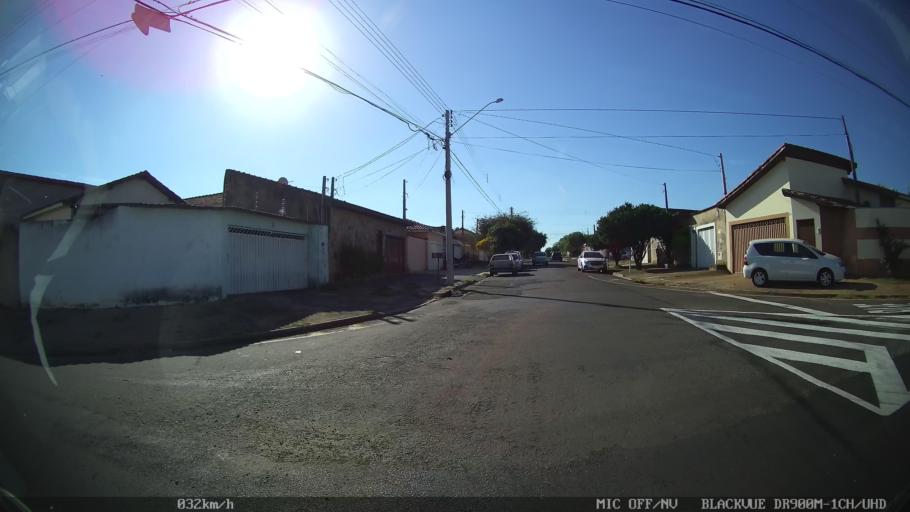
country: BR
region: Sao Paulo
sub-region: Franca
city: Franca
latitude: -20.5115
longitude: -47.4228
